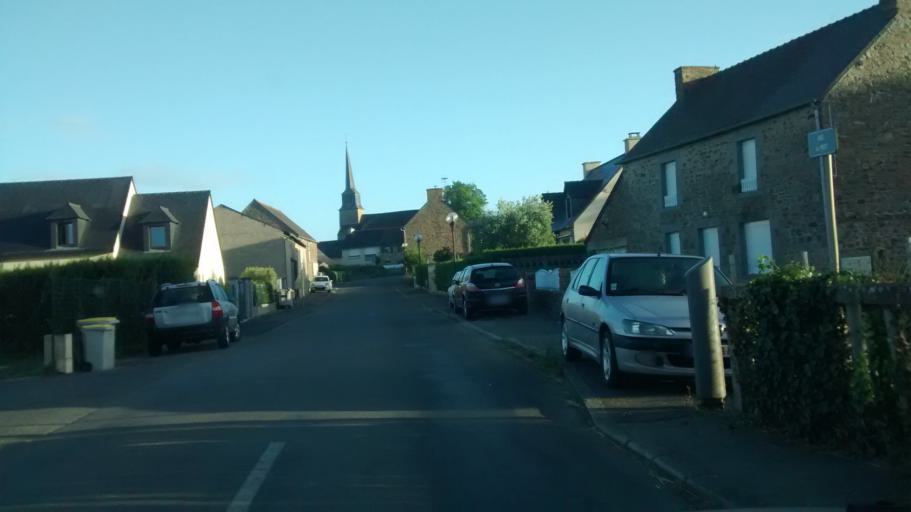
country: FR
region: Brittany
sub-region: Departement d'Ille-et-Vilaine
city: La Gouesniere
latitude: 48.5738
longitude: -1.8820
